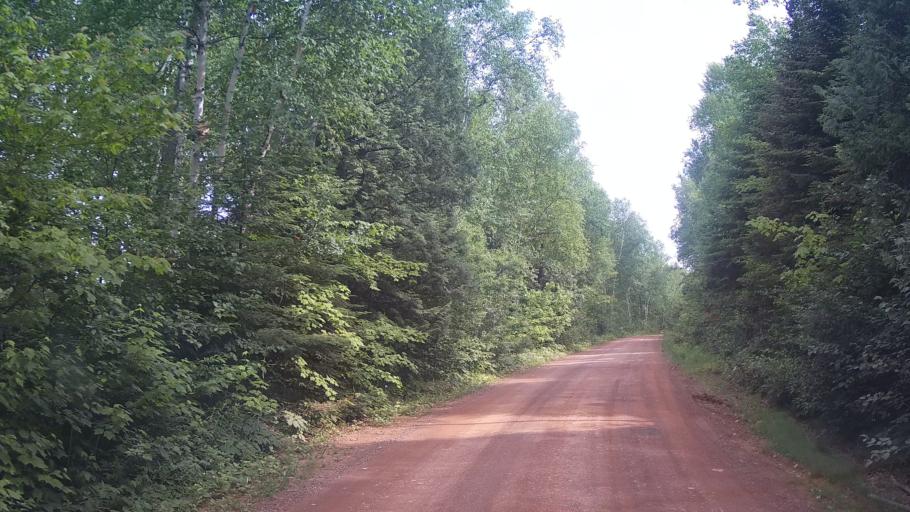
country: CA
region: Ontario
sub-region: Thunder Bay District
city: Thunder Bay
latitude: 48.6754
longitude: -88.6677
